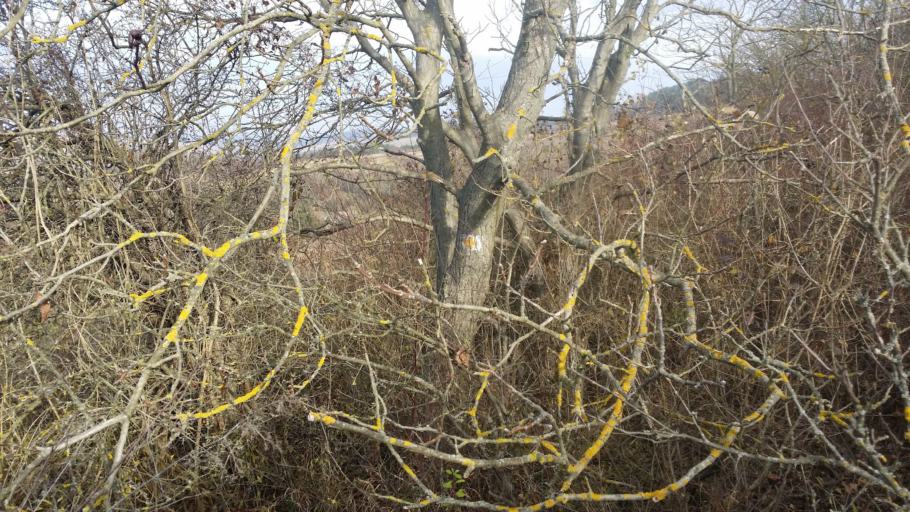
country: HU
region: Tolna
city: Bonyhad
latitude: 46.2341
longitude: 18.5878
